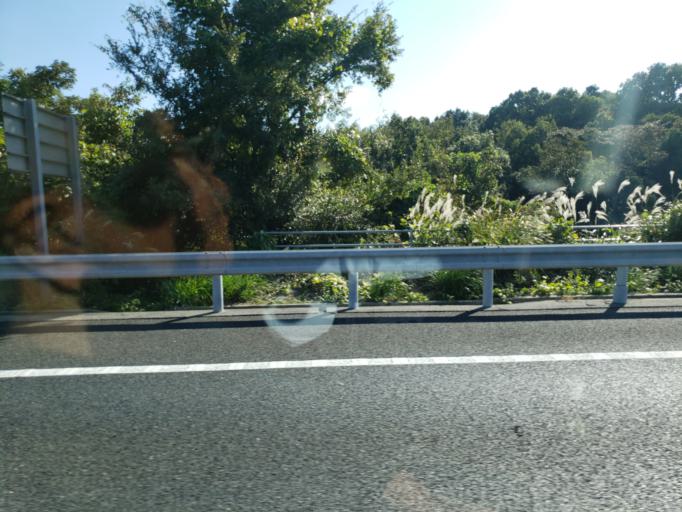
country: JP
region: Hyogo
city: Sumoto
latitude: 34.3528
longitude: 134.8525
